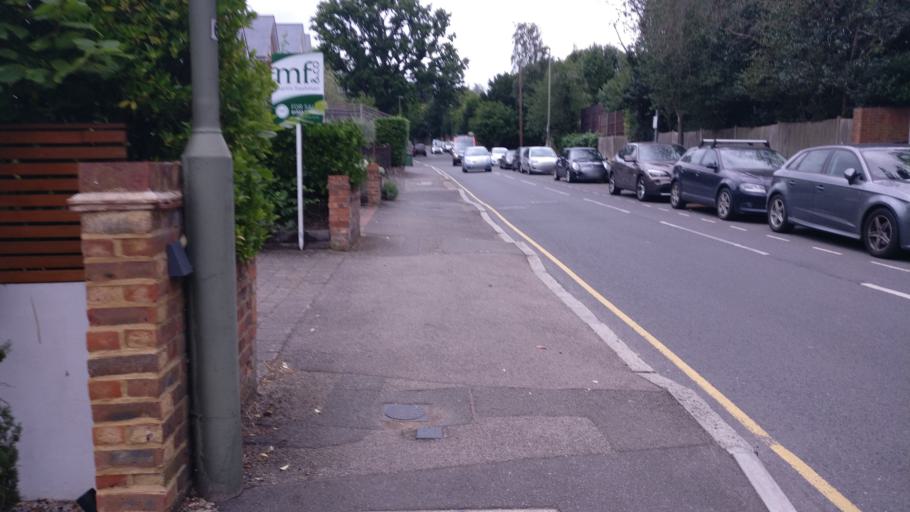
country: GB
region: England
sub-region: Surrey
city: Weybridge
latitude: 51.3719
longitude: -0.4551
